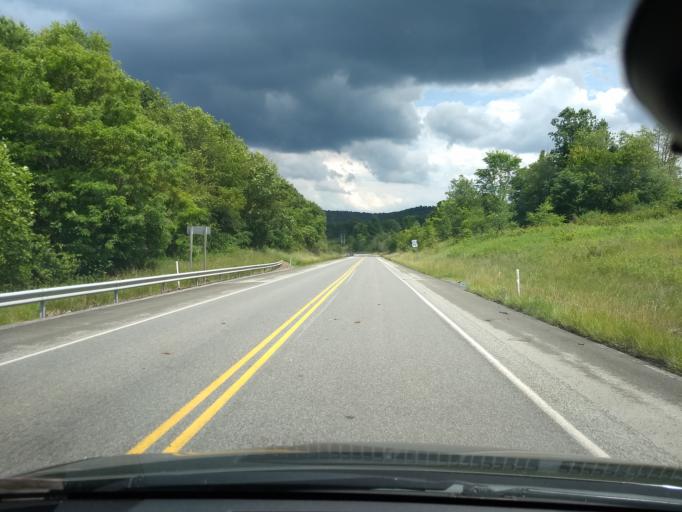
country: US
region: Pennsylvania
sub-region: Westmoreland County
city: Avonmore
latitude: 40.5191
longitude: -79.5018
